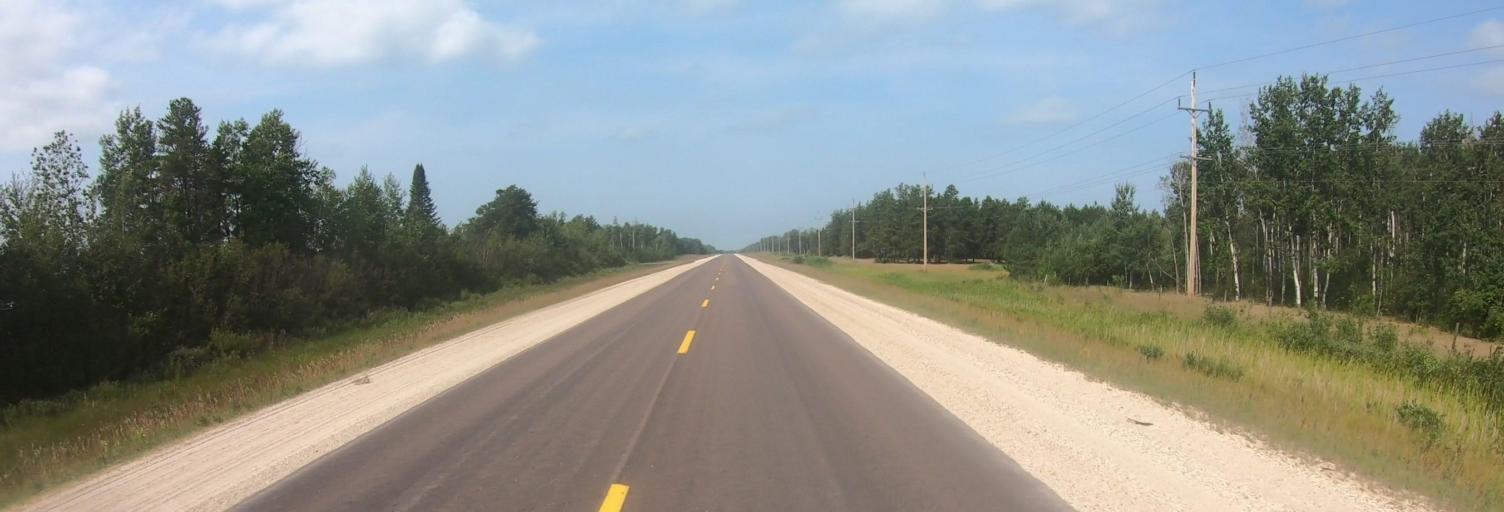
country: CA
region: Manitoba
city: La Broquerie
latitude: 49.2669
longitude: -96.4262
